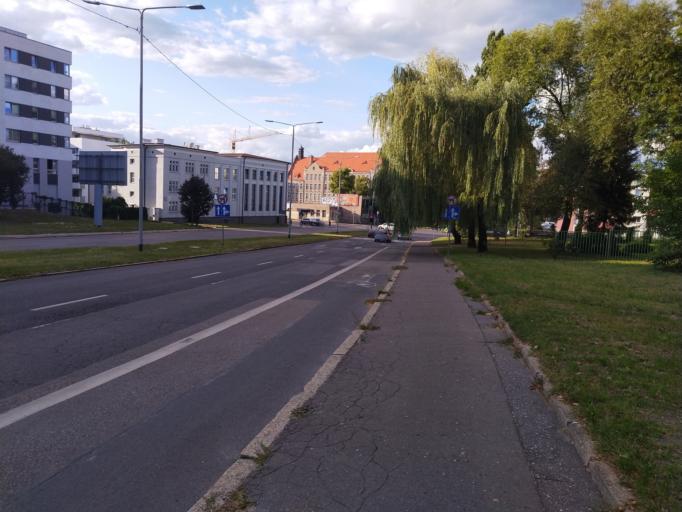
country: PL
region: West Pomeranian Voivodeship
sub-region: Szczecin
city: Szczecin
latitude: 53.4386
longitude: 14.5637
